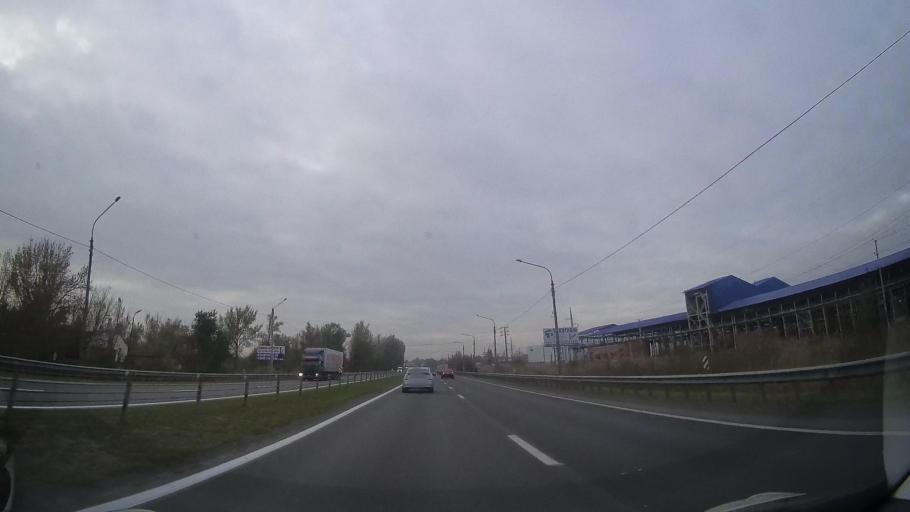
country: RU
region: Rostov
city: Bataysk
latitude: 47.1158
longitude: 39.7687
